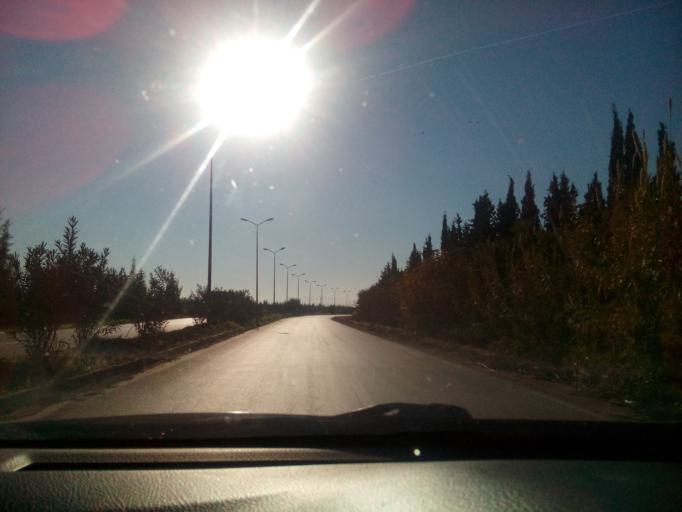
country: DZ
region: Relizane
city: Relizane
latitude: 35.7267
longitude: 0.5880
